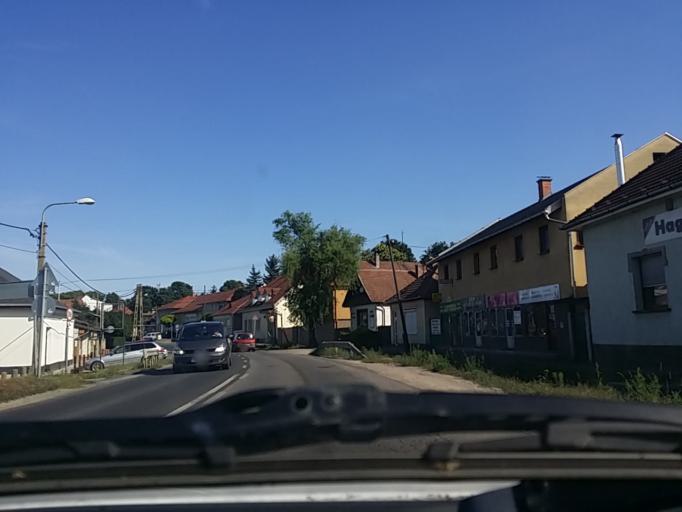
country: HU
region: Pest
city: Pilisvorosvar
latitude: 47.6173
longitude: 18.9143
